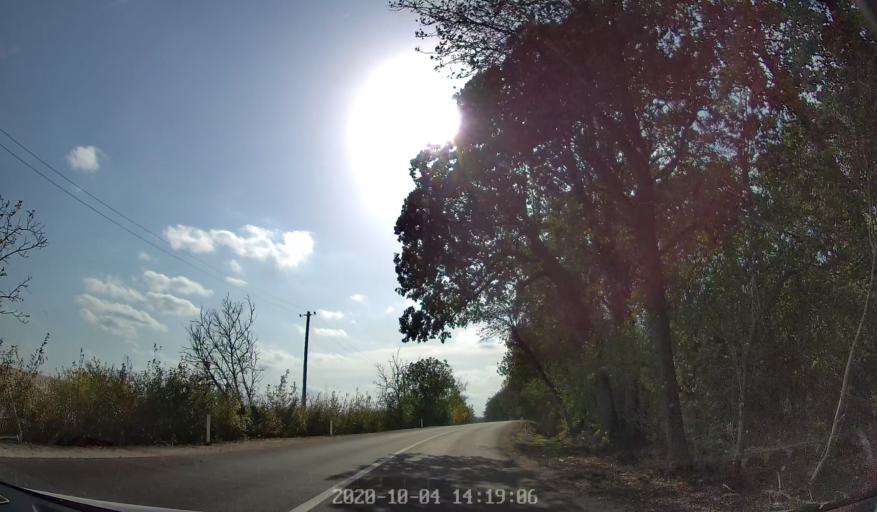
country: MD
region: Rezina
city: Saharna
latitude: 47.5937
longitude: 28.9762
